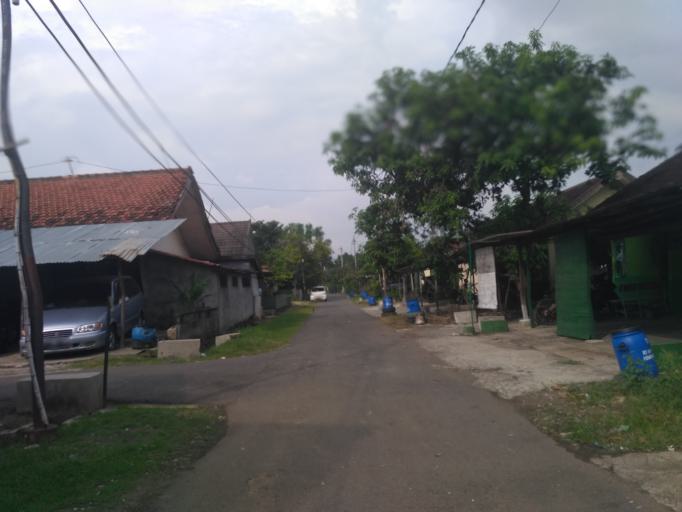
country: ID
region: Central Java
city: Semarang
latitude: -6.9903
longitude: 110.3728
